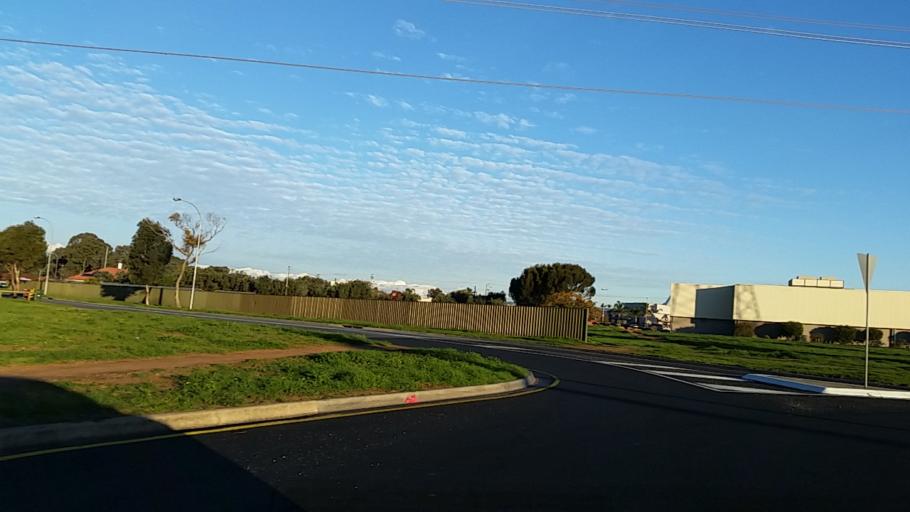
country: AU
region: South Australia
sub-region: Salisbury
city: Salisbury
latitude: -34.7652
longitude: 138.6233
